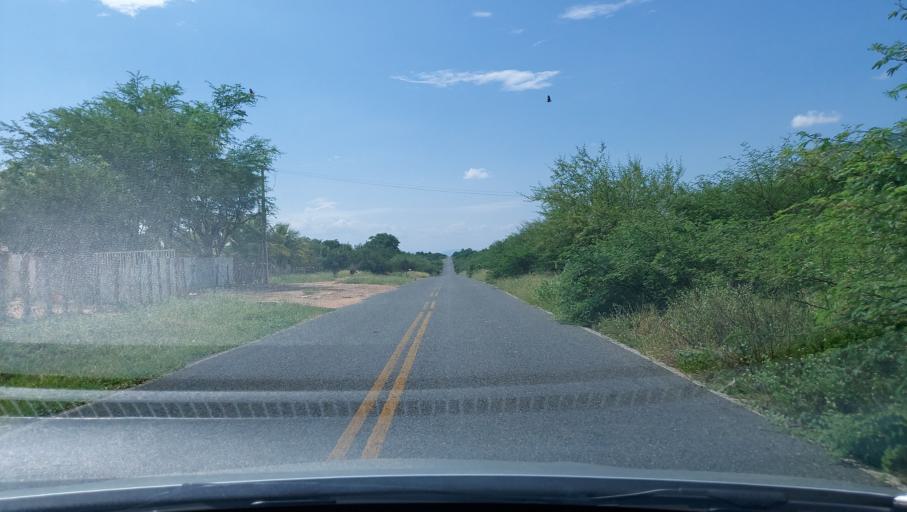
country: BR
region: Bahia
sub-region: Oliveira Dos Brejinhos
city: Beira Rio
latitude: -12.1479
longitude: -42.5548
